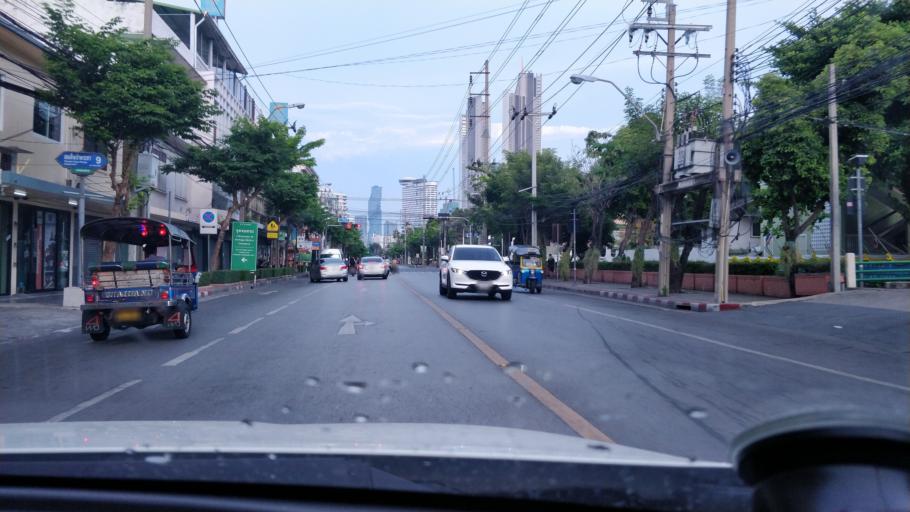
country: TH
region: Bangkok
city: Khlong San
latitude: 13.7326
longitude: 100.5015
